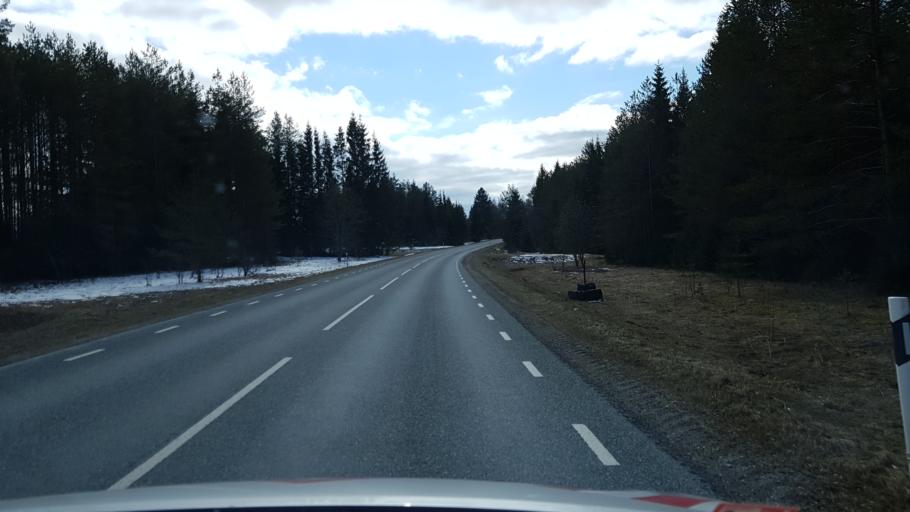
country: EE
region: Laeaene-Virumaa
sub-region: Tapa vald
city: Tapa
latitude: 59.2875
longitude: 25.9971
